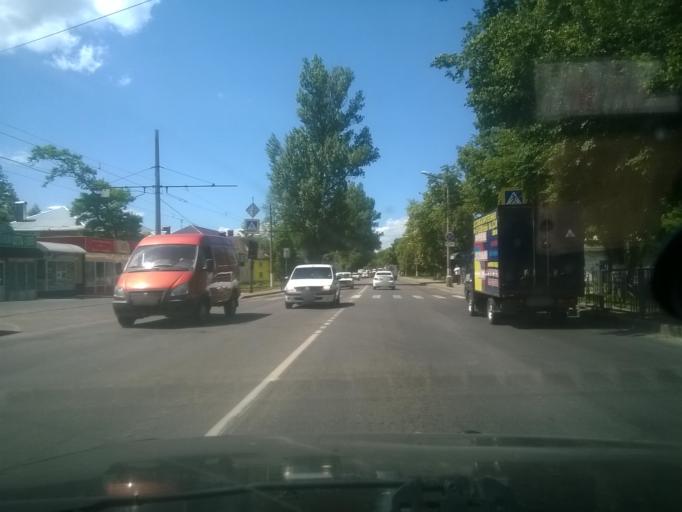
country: RU
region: Kursk
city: Voroshnevo
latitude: 51.6670
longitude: 36.1026
